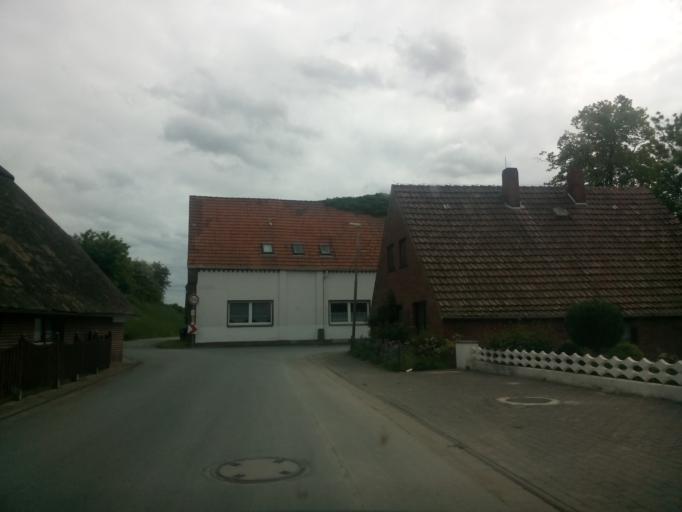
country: DE
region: Lower Saxony
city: Lemwerder
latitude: 53.1511
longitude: 8.6151
